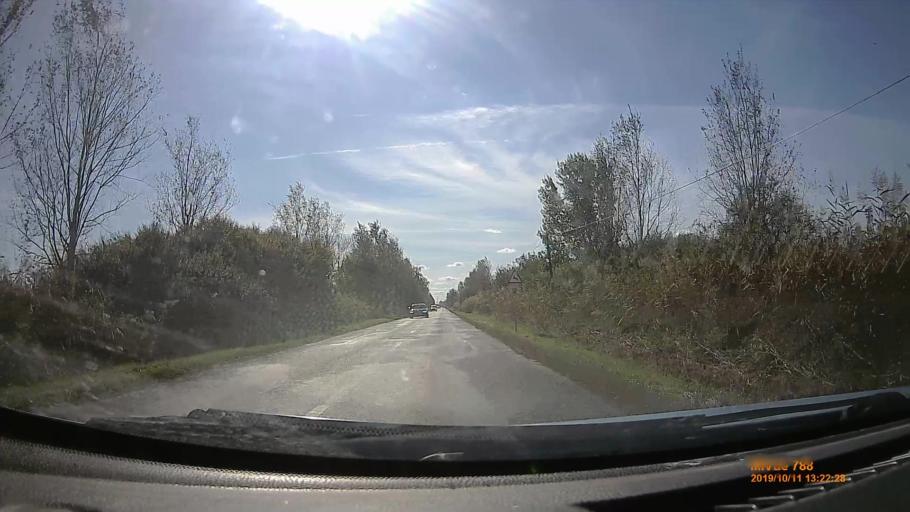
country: HU
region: Hajdu-Bihar
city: Balmazujvaros
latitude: 47.5490
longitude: 21.3248
